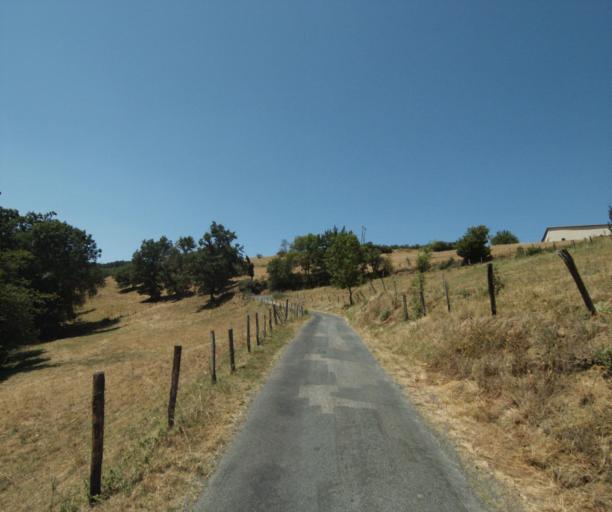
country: FR
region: Rhone-Alpes
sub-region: Departement du Rhone
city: Bessenay
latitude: 45.7732
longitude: 4.5406
